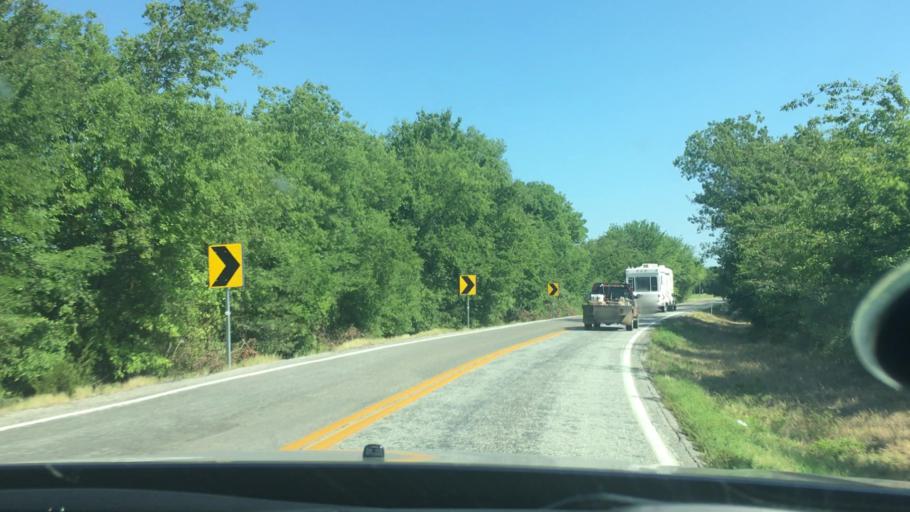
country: US
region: Oklahoma
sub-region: Johnston County
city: Tishomingo
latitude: 34.1997
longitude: -96.5427
